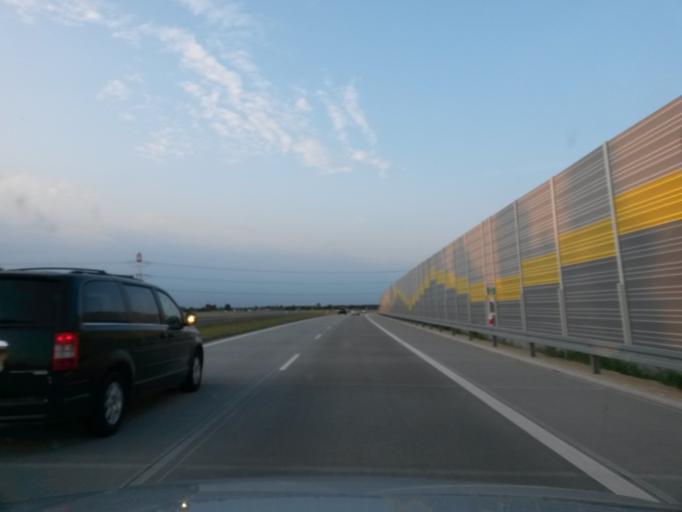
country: PL
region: Lodz Voivodeship
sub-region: Powiat sieradzki
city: Zloczew
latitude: 51.3821
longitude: 18.5535
